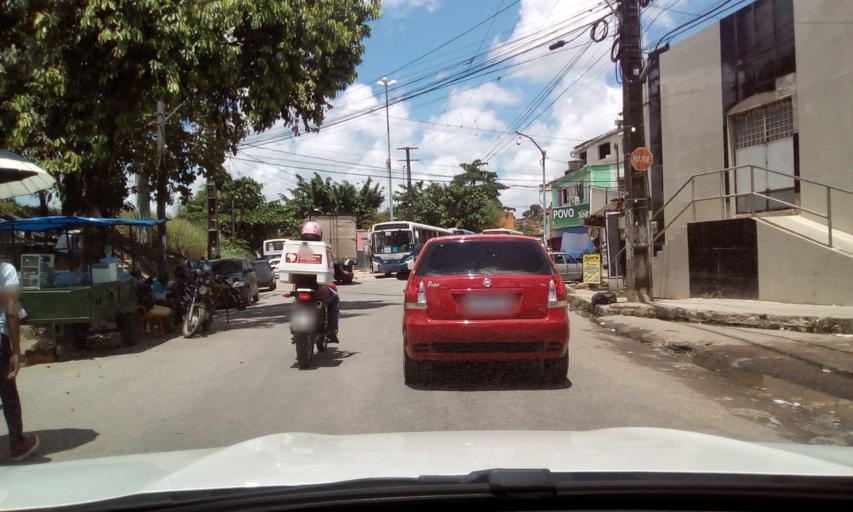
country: BR
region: Pernambuco
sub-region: Sao Lourenco Da Mata
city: Sao Lourenco da Mata
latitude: -7.9937
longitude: -34.9372
